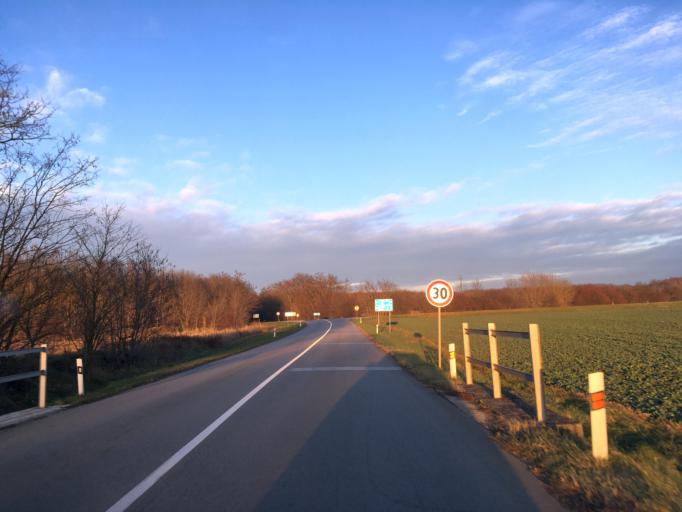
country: SK
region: Nitriansky
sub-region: Okres Komarno
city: Hurbanovo
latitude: 47.9231
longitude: 18.2334
